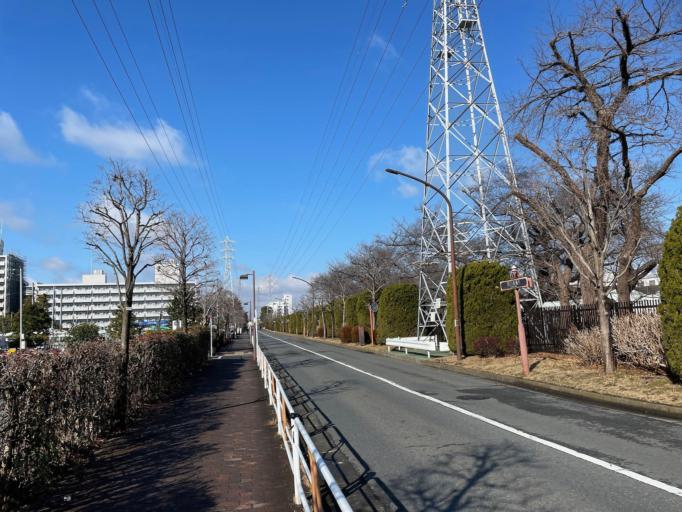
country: JP
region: Tokyo
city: Kokubunji
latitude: 35.6792
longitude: 139.4662
